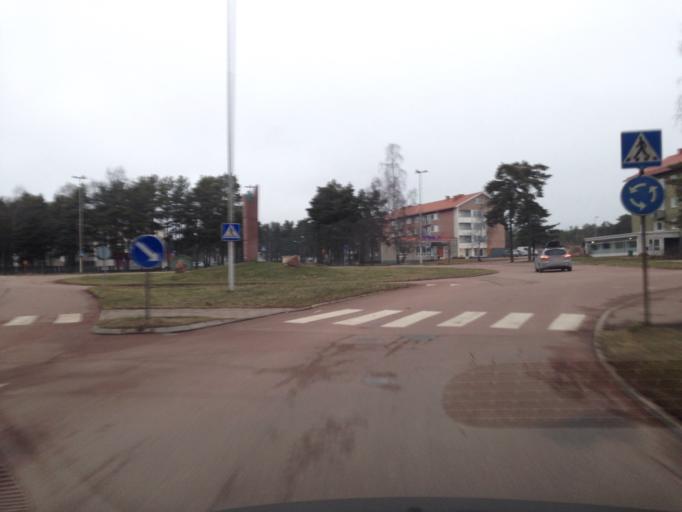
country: AX
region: Mariehamns stad
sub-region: Mariehamn
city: Mariehamn
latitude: 60.1042
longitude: 19.9371
